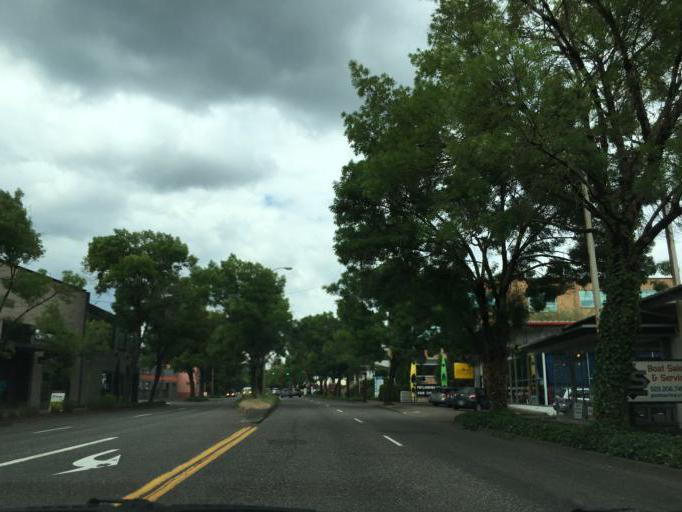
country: US
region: Oregon
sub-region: Clackamas County
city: Milwaukie
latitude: 45.4759
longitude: -122.6718
